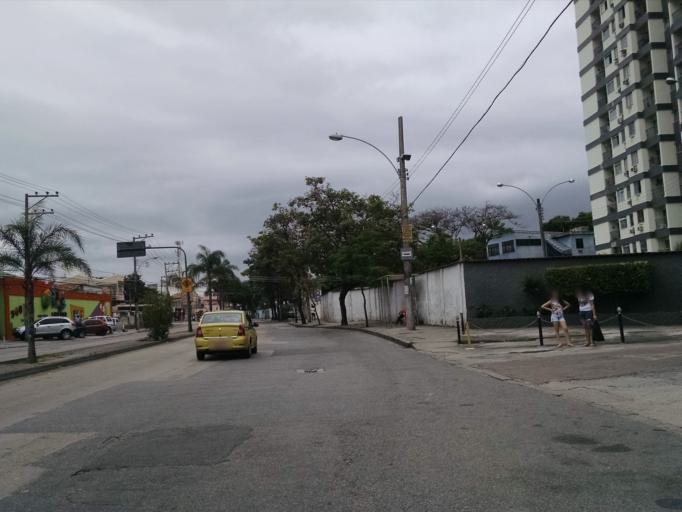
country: BR
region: Rio de Janeiro
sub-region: Duque De Caxias
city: Duque de Caxias
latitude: -22.8416
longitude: -43.3181
